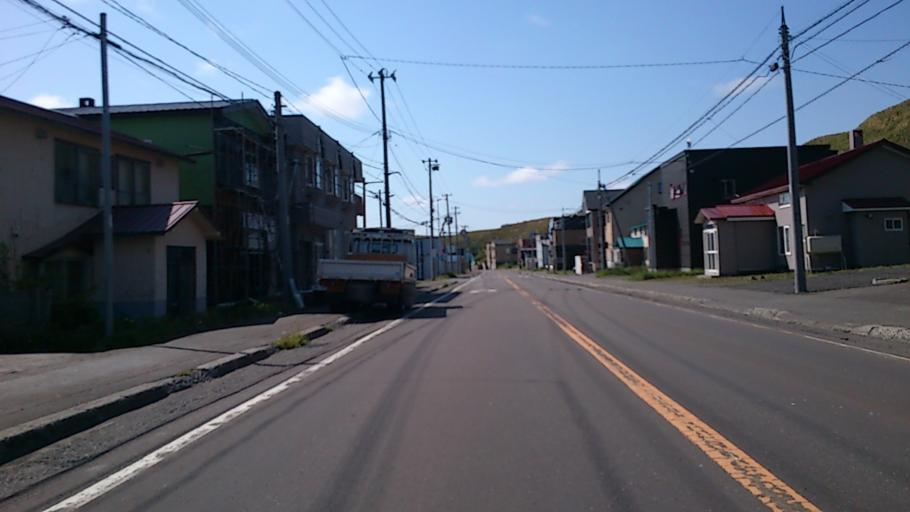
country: JP
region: Hokkaido
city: Makubetsu
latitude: 45.5193
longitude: 141.9414
